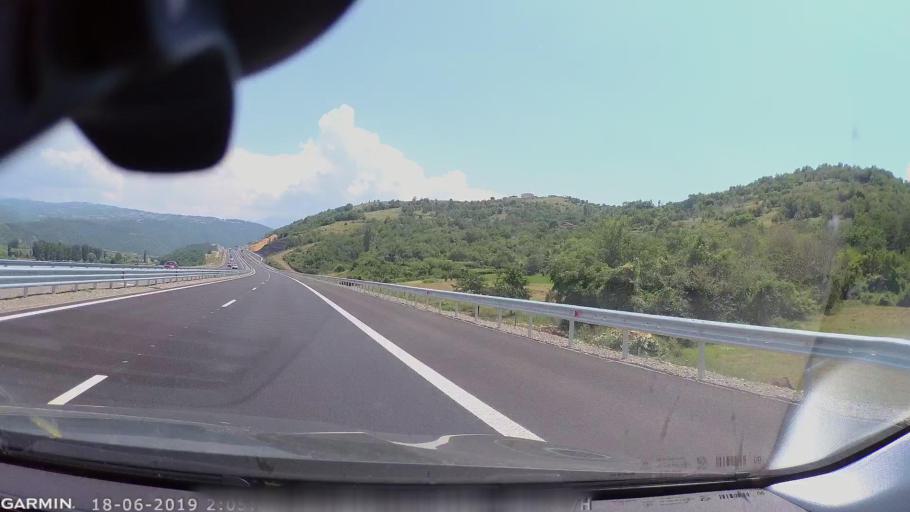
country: BG
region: Blagoevgrad
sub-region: Obshtina Blagoevgrad
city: Blagoevgrad
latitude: 41.9787
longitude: 23.0662
